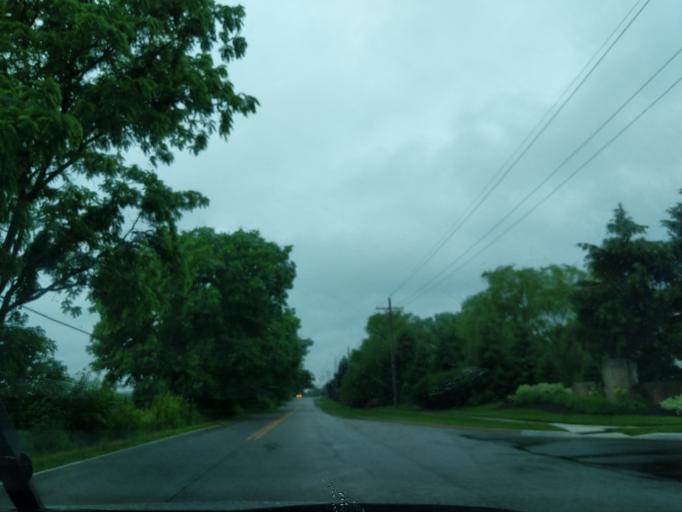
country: US
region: Indiana
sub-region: Hamilton County
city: Noblesville
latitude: 40.0658
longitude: -85.9823
